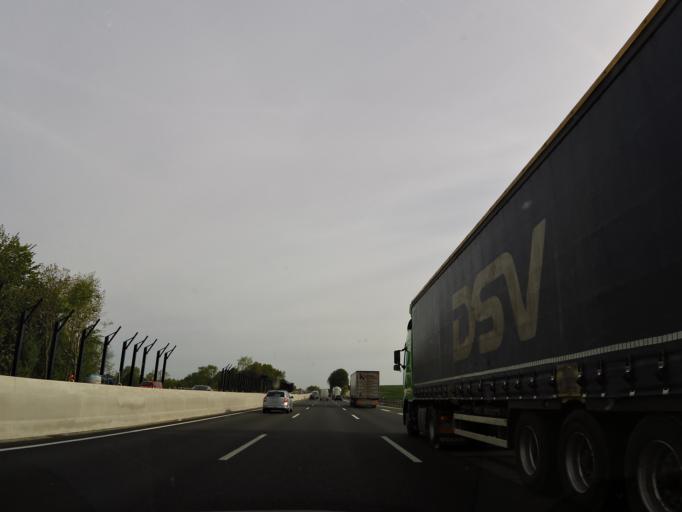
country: DE
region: Lower Saxony
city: Seesen
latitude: 51.8872
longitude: 10.1306
